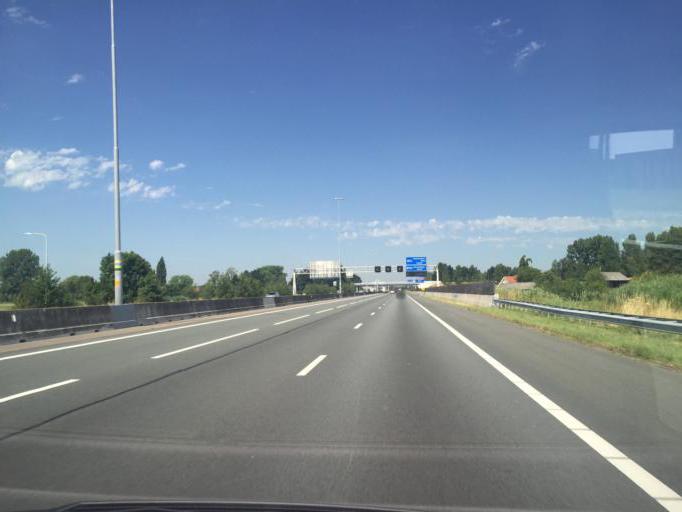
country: NL
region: Gelderland
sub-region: Gemeente Ede
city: Ederveen
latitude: 52.0312
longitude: 5.5991
